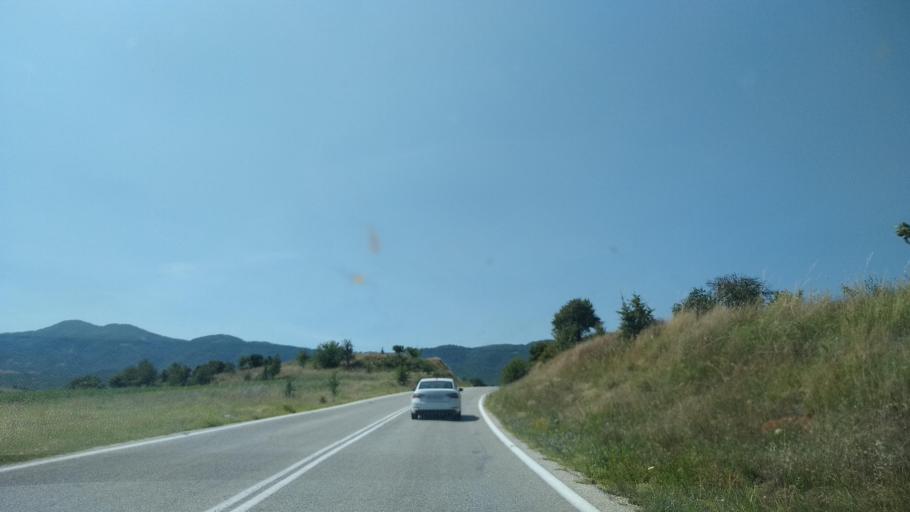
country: GR
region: Central Macedonia
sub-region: Nomos Thessalonikis
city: Nea Apollonia
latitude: 40.5191
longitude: 23.4728
